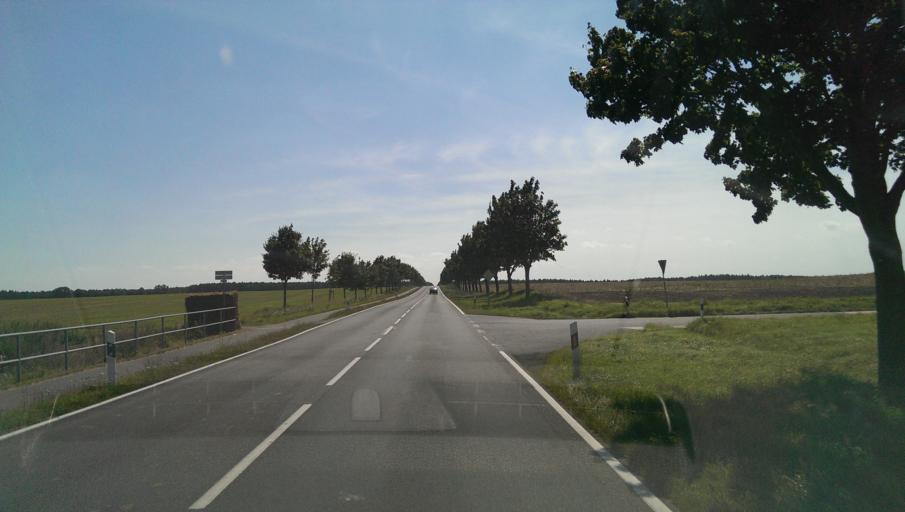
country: DE
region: Saxony-Anhalt
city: Kropstadt
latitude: 51.9971
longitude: 12.7723
